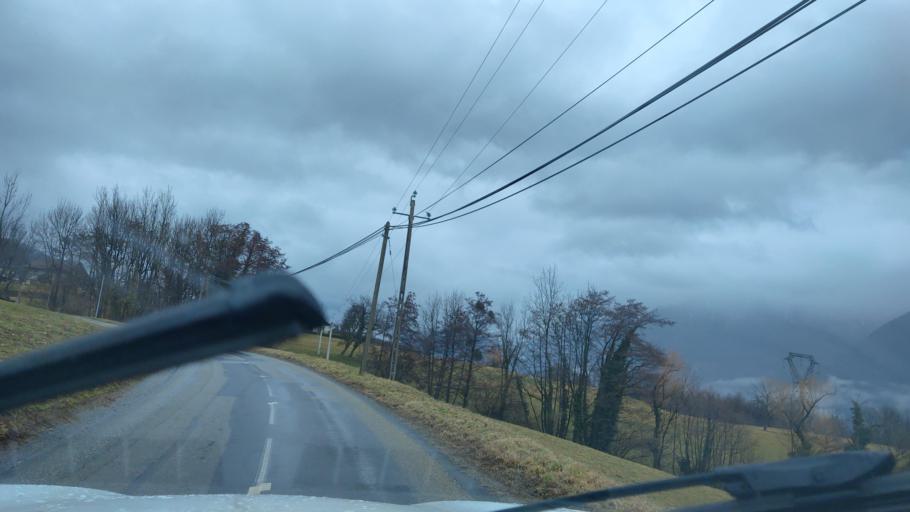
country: FR
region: Rhone-Alpes
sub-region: Departement de la Savoie
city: Aiton
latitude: 45.4959
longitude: 6.2826
